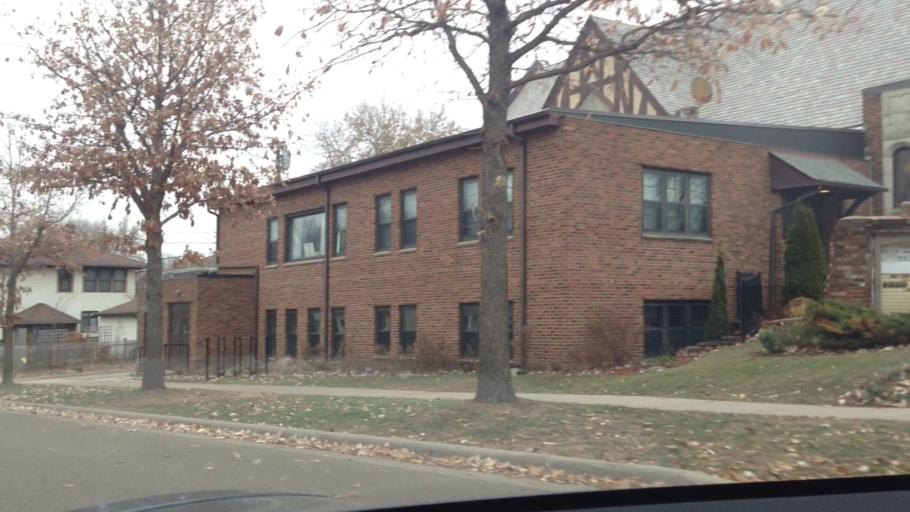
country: US
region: Minnesota
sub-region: Ramsey County
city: Falcon Heights
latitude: 44.9362
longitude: -93.1823
